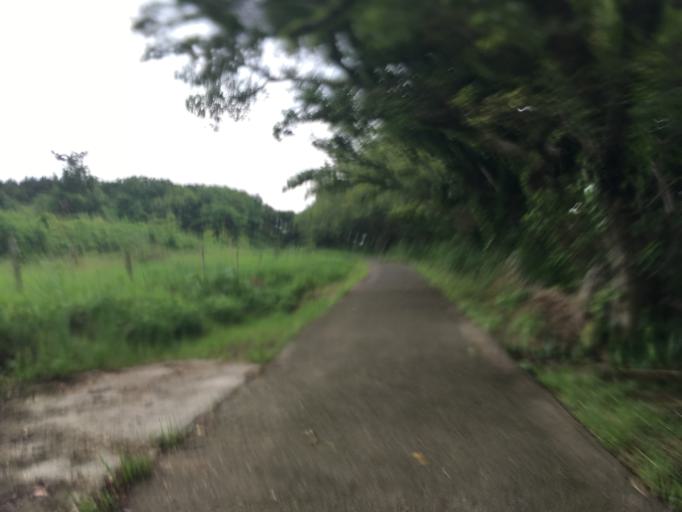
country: JP
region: Aichi
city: Ishiki
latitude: 34.7170
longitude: 137.0495
